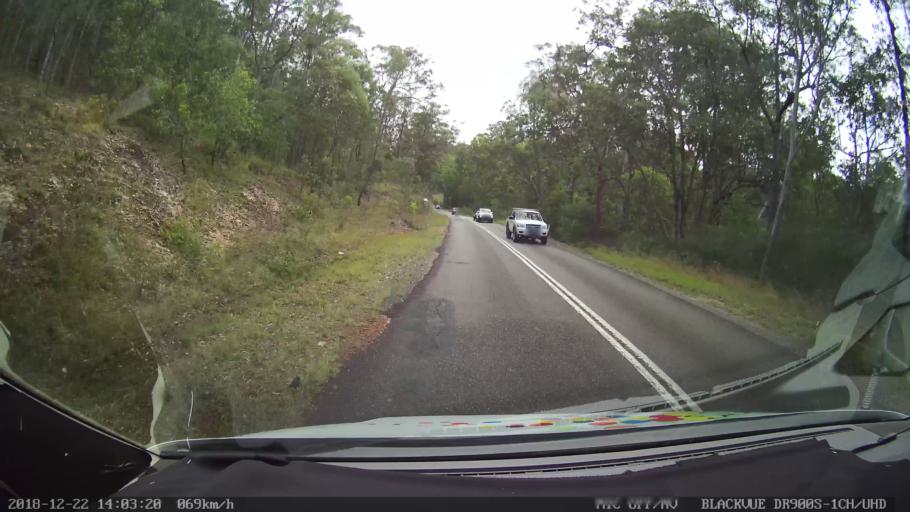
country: AU
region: New South Wales
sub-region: Clarence Valley
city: Coutts Crossing
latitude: -29.9284
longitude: 152.7392
